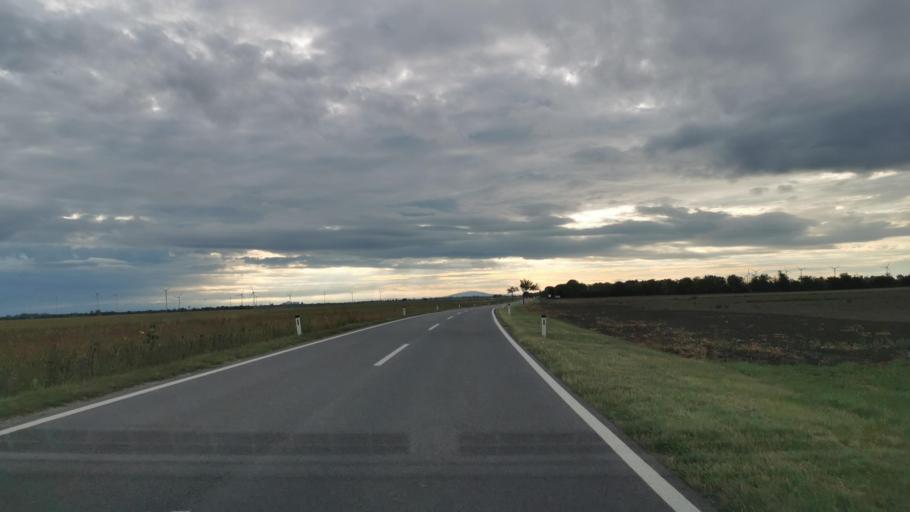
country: AT
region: Lower Austria
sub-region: Politischer Bezirk Ganserndorf
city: Grosshofen
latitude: 48.2311
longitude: 16.6082
